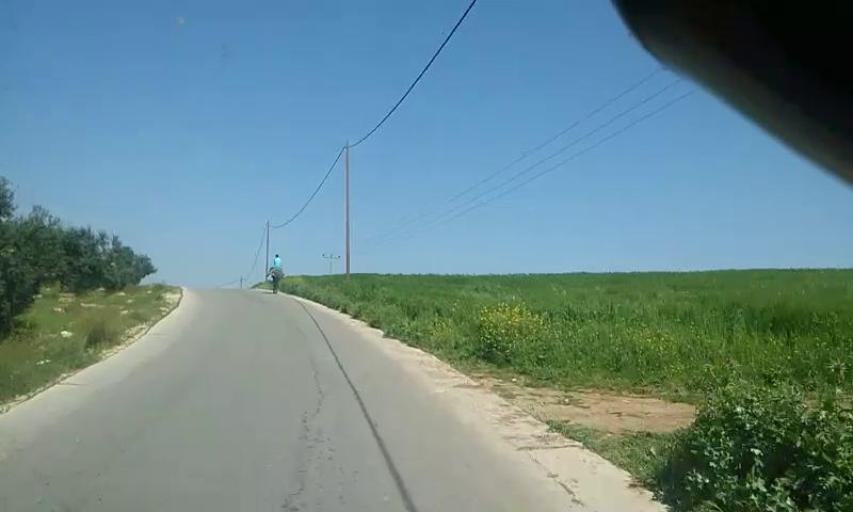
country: PS
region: West Bank
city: Dayr al `Asal al Fawqa
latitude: 31.4699
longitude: 34.9453
